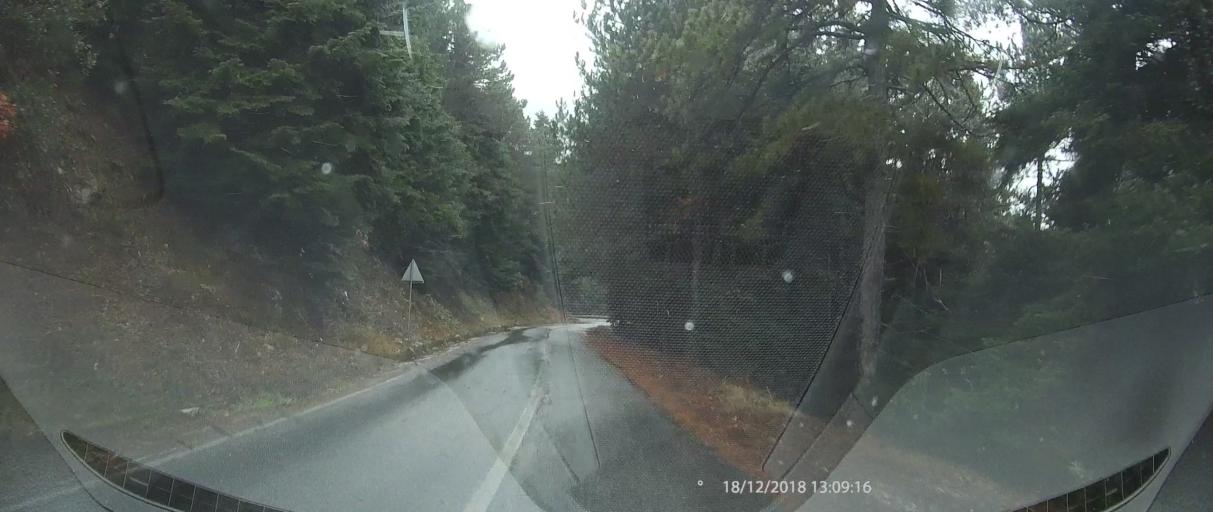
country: GR
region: Central Macedonia
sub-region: Nomos Pierias
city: Litochoro
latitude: 40.1055
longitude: 22.4796
